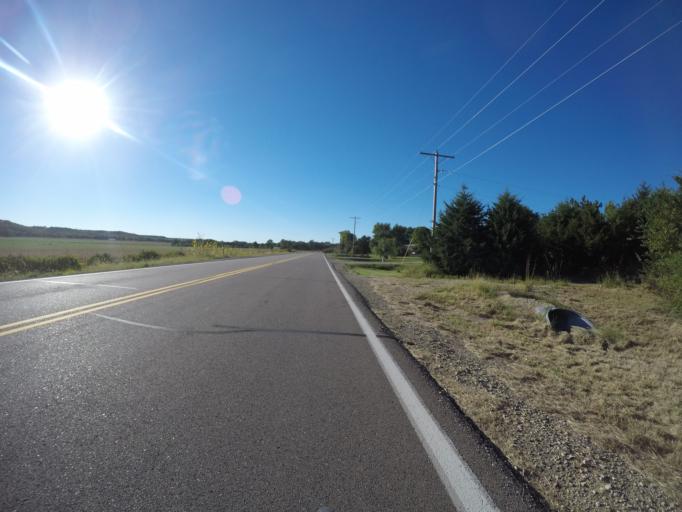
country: US
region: Kansas
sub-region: Riley County
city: Ogden
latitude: 39.2139
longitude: -96.6851
